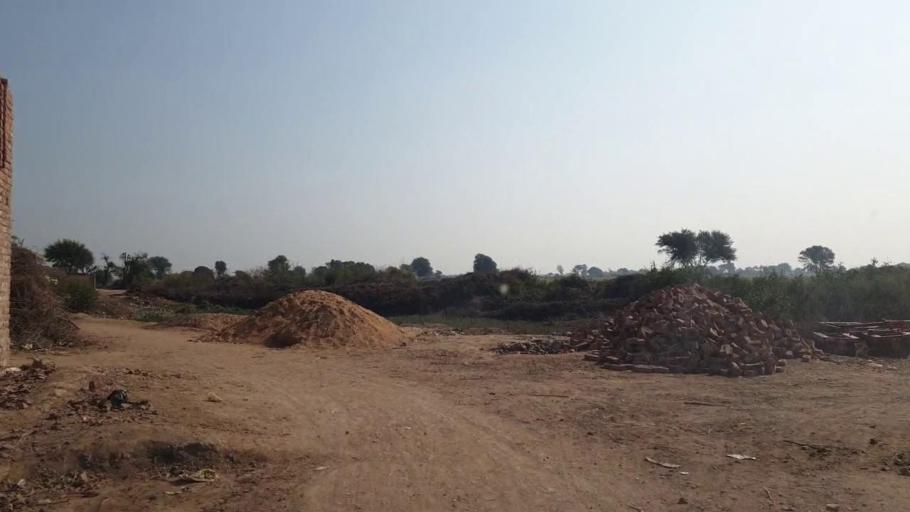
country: PK
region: Sindh
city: Hala
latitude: 25.9174
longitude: 68.3986
